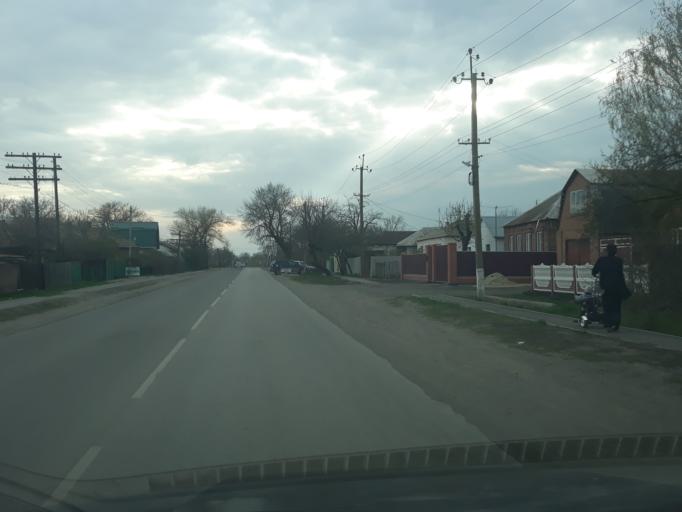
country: RU
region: Rostov
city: Novobessergenovka
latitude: 47.1723
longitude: 38.7541
